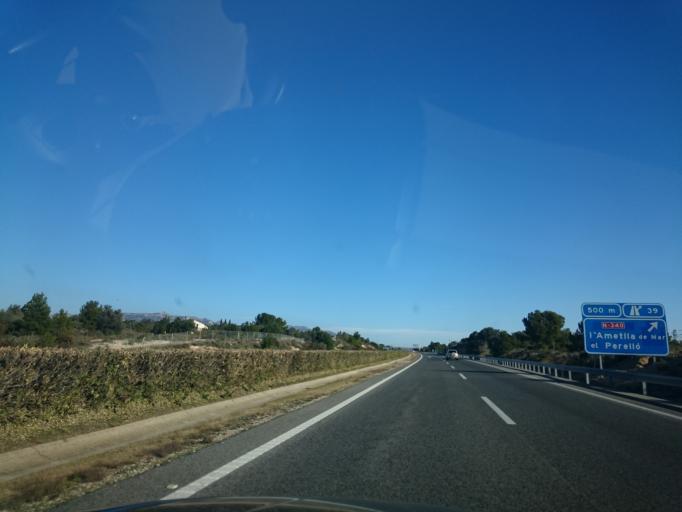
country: ES
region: Catalonia
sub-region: Provincia de Tarragona
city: l'Ametlla de Mar
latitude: 40.8769
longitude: 0.7898
